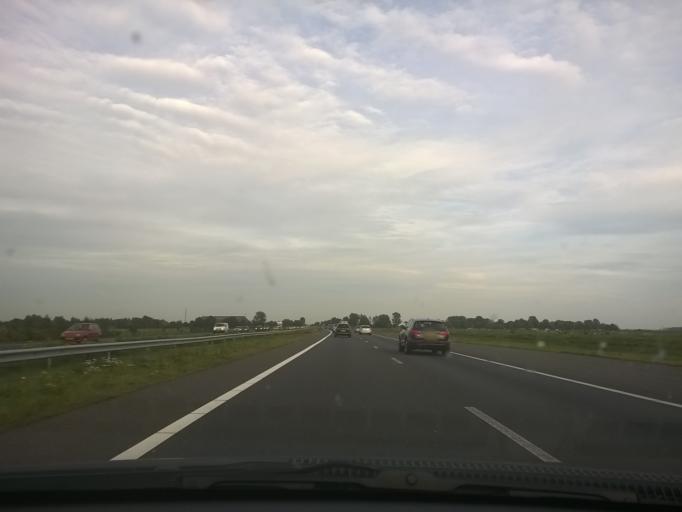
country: NL
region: Groningen
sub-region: Gemeente Zuidhorn
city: Zuidhorn
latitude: 53.1953
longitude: 6.4349
